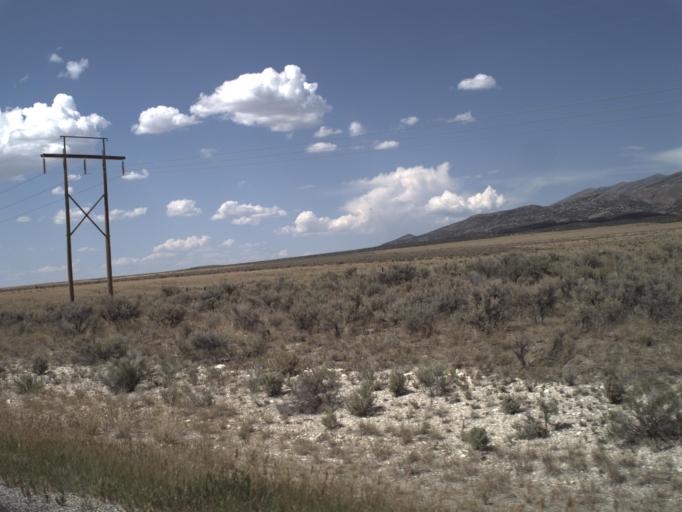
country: US
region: Idaho
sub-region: Minidoka County
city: Rupert
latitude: 41.9918
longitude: -113.1857
